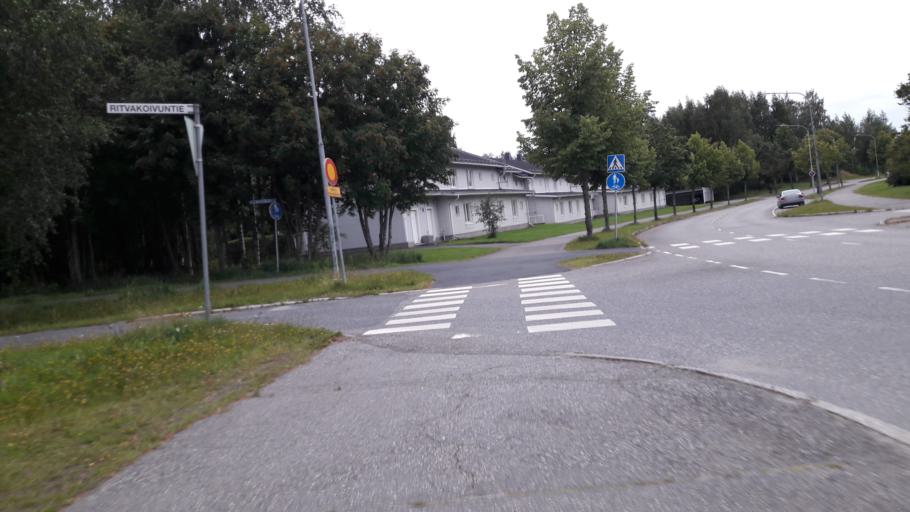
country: FI
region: North Karelia
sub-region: Joensuu
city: Joensuu
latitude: 62.6175
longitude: 29.6947
